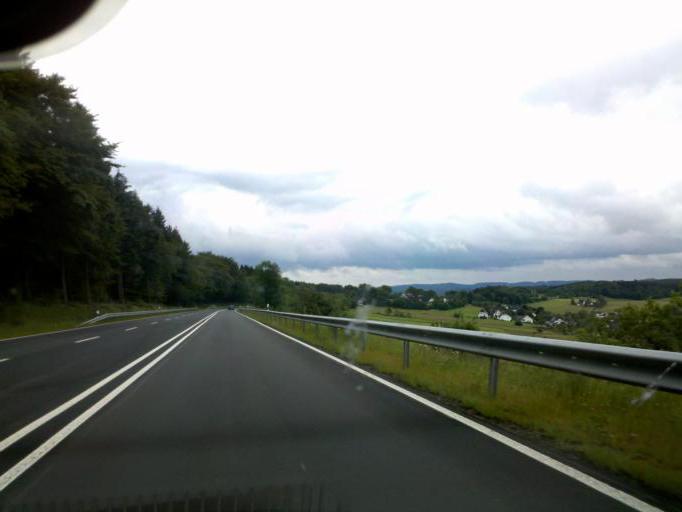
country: DE
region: North Rhine-Westphalia
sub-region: Regierungsbezirk Arnsberg
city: Olpe
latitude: 51.0512
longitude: 7.8964
